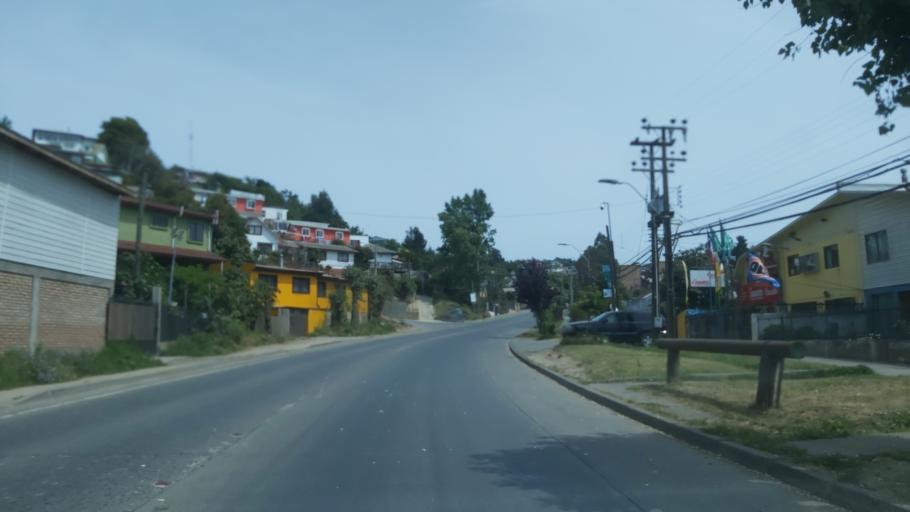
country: CL
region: Maule
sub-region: Provincia de Talca
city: Constitucion
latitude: -35.3342
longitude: -72.4163
